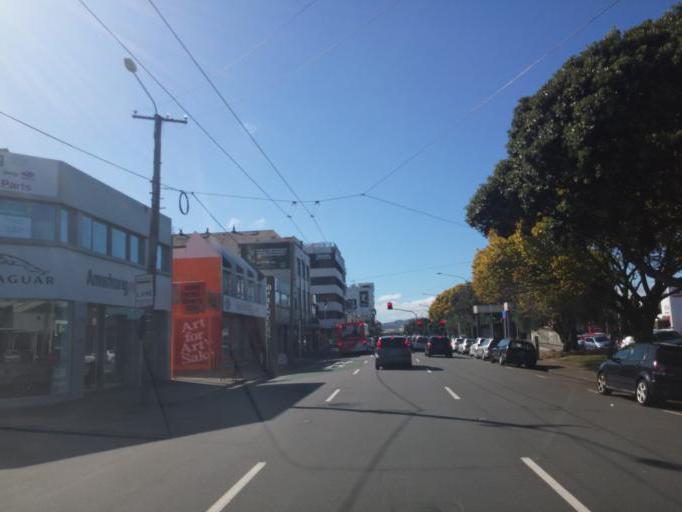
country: NZ
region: Wellington
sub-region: Wellington City
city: Wellington
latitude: -41.2979
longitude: 174.7815
